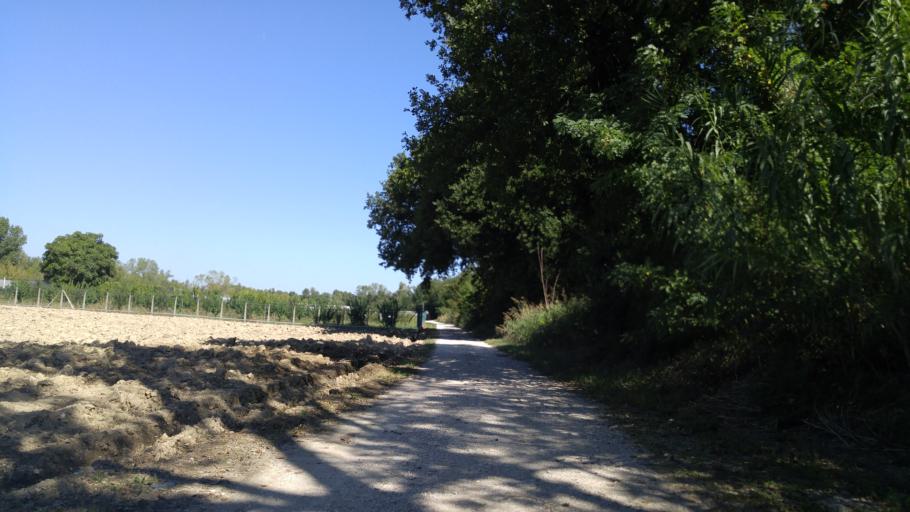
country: IT
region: The Marches
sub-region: Provincia di Pesaro e Urbino
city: Villanova
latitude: 43.7535
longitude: 12.9368
